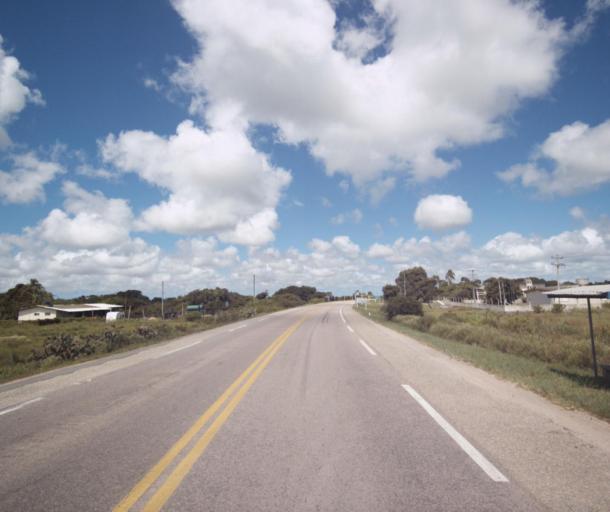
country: BR
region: Rio Grande do Sul
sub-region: Arroio Grande
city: Arroio Grande
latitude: -32.5374
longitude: -52.5381
